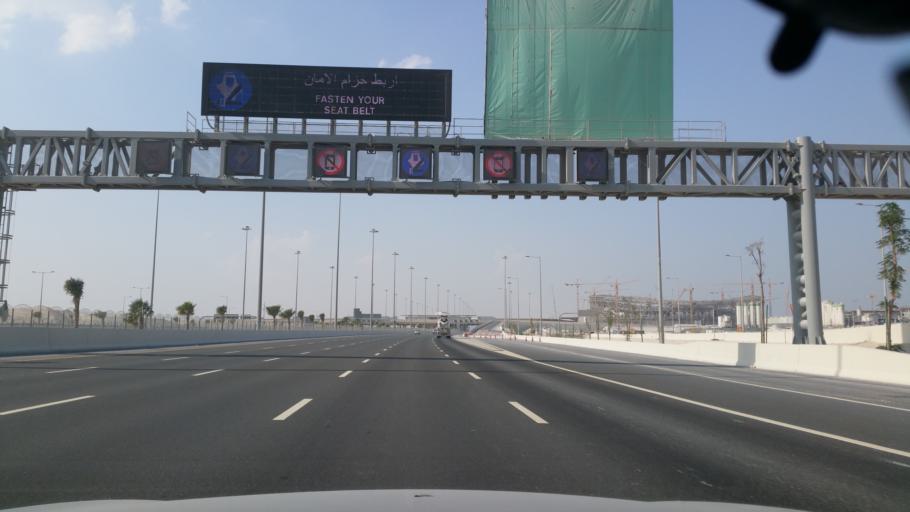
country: QA
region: Baladiyat Umm Salal
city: Umm Salal Muhammad
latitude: 25.4075
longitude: 51.4901
